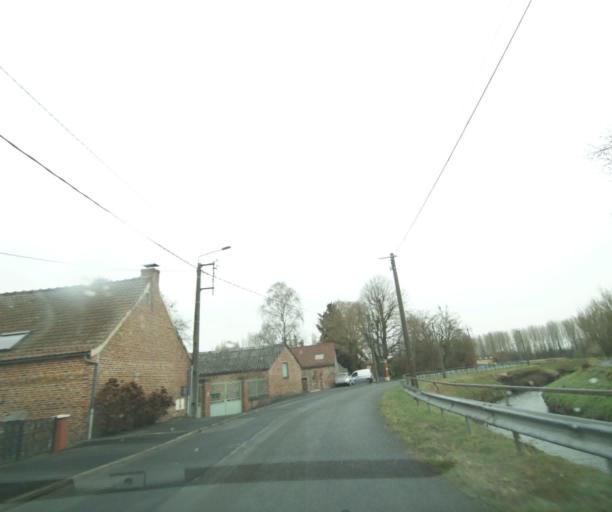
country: BE
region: Wallonia
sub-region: Province du Hainaut
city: Bernissart
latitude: 50.4424
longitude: 3.6301
